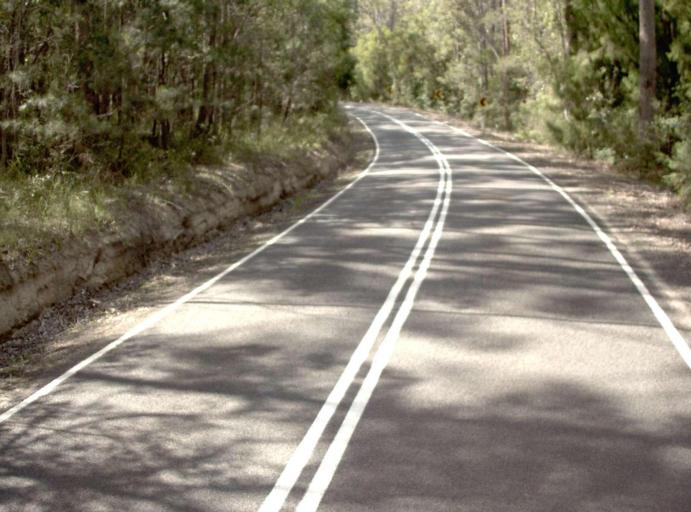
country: AU
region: New South Wales
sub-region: Bega Valley
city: Eden
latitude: -37.5251
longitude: 149.6892
